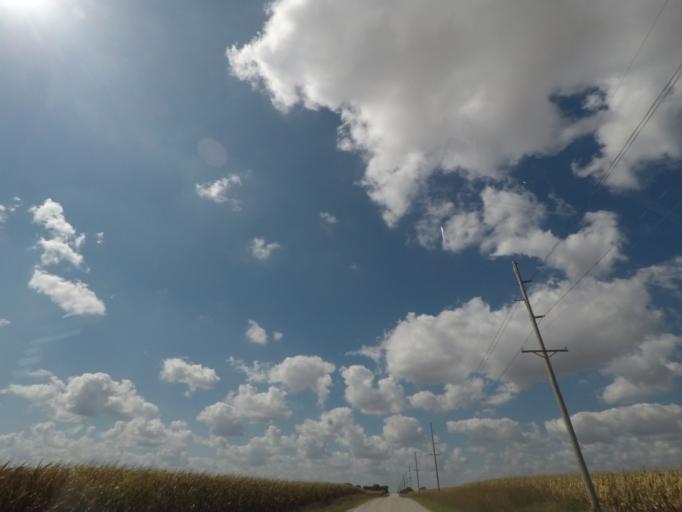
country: US
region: Iowa
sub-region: Story County
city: Nevada
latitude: 42.0344
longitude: -93.4009
